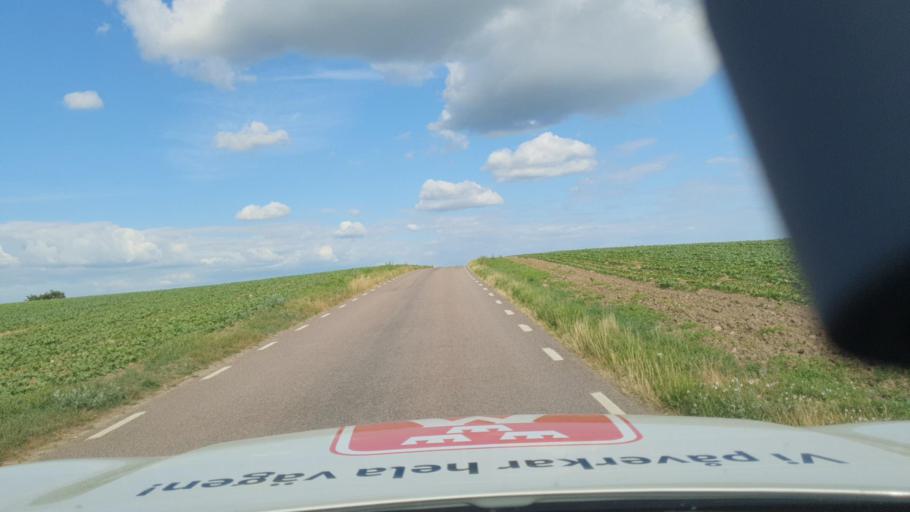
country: SE
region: Skane
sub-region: Skurups Kommun
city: Rydsgard
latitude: 55.4508
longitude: 13.5787
